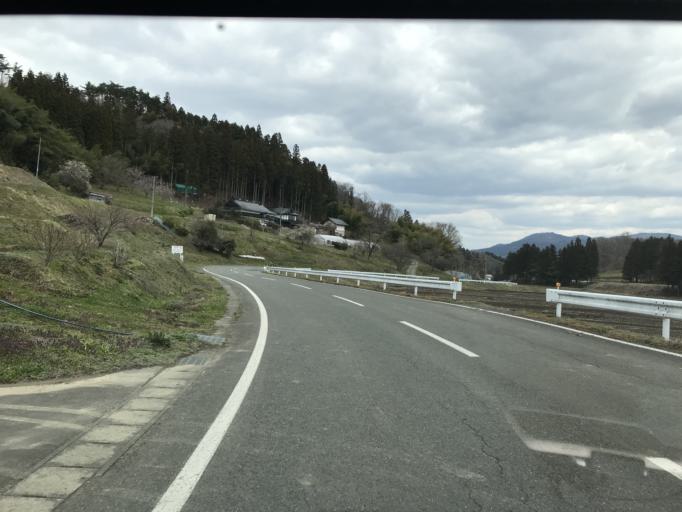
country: JP
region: Iwate
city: Ichinoseki
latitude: 38.9657
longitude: 141.0953
